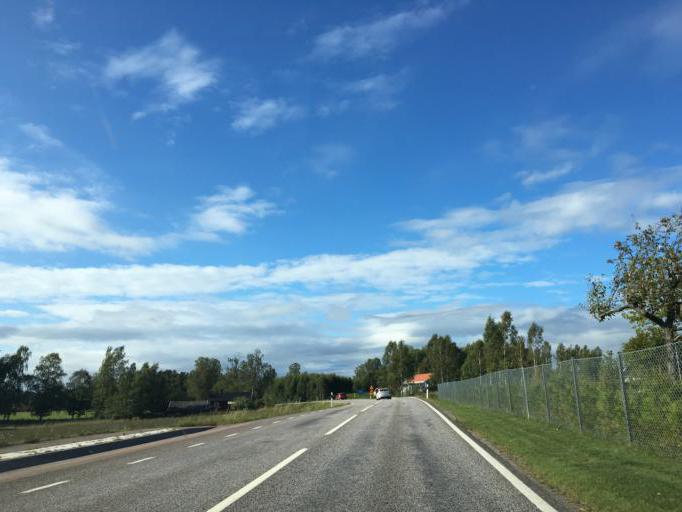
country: SE
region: Soedermanland
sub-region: Nykopings Kommun
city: Stigtomta
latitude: 58.8693
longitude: 16.8994
